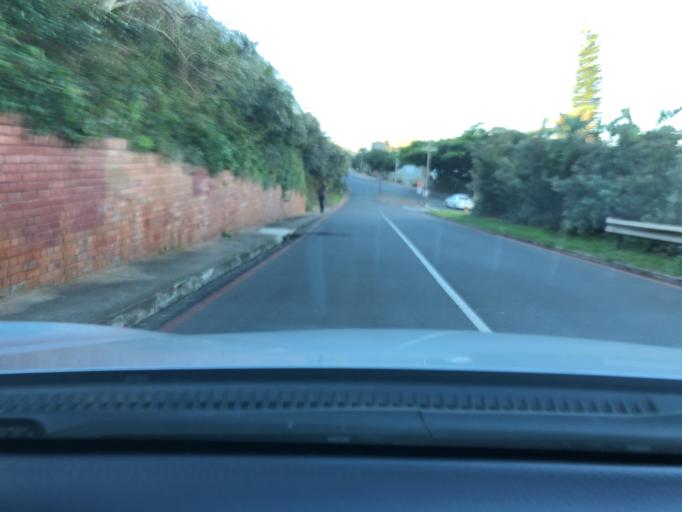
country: ZA
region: KwaZulu-Natal
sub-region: eThekwini Metropolitan Municipality
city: Umkomaas
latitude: -30.0446
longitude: 30.8928
